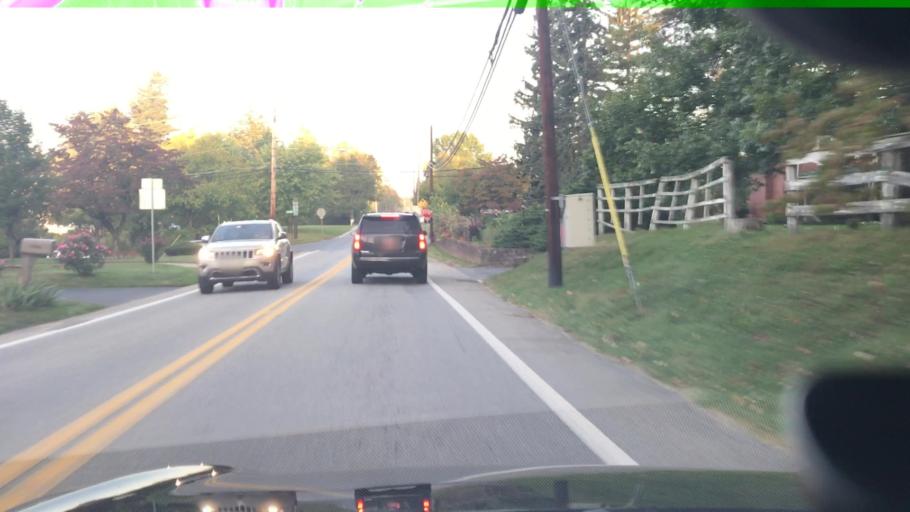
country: US
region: Pennsylvania
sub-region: Cumberland County
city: Lower Allen
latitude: 40.1683
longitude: -76.9203
